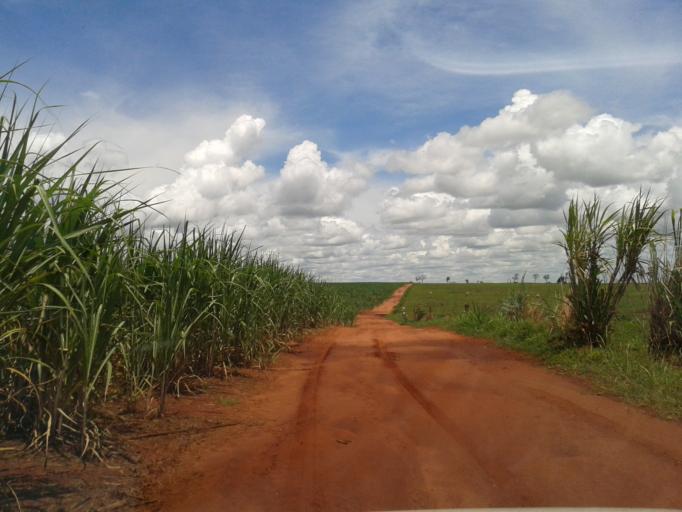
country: BR
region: Minas Gerais
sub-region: Santa Vitoria
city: Santa Vitoria
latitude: -19.1994
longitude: -50.6652
